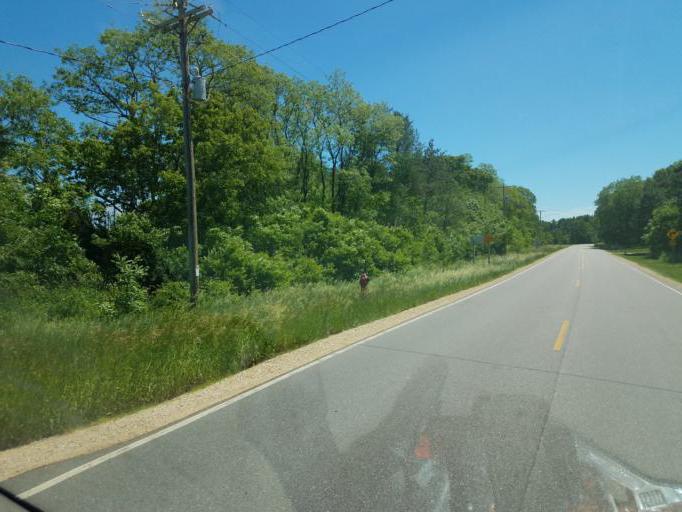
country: US
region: Wisconsin
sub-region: Juneau County
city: New Lisbon
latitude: 43.9162
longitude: -90.2649
